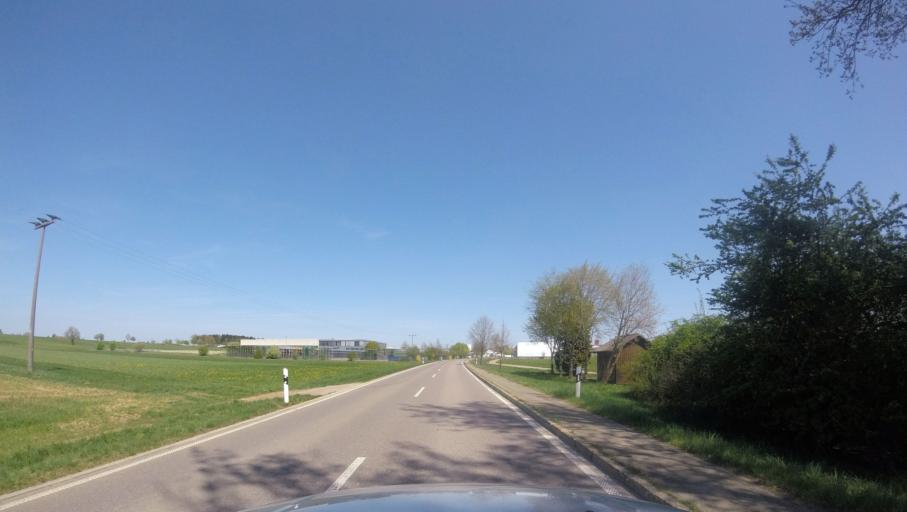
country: DE
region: Baden-Wuerttemberg
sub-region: Regierungsbezirk Stuttgart
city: Durlangen
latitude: 48.8524
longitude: 9.7865
